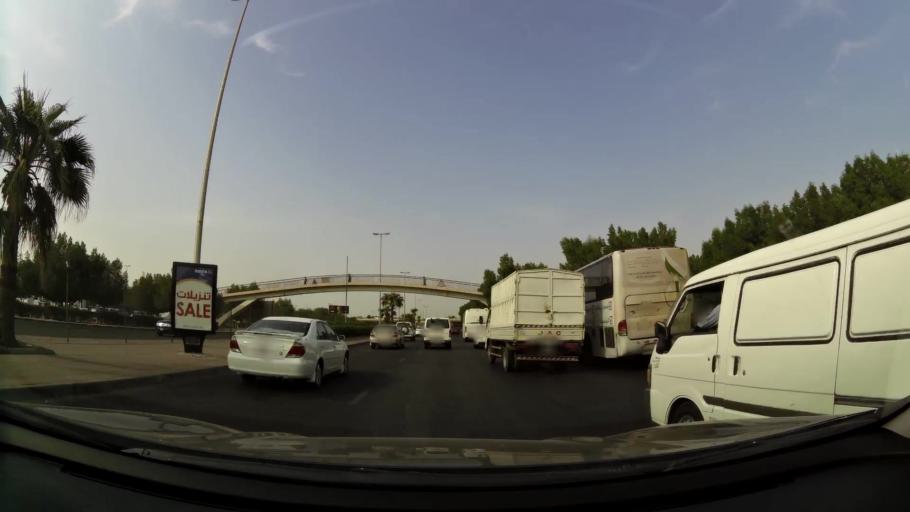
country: KW
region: Al Asimah
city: Ash Shamiyah
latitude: 29.3139
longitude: 47.9616
